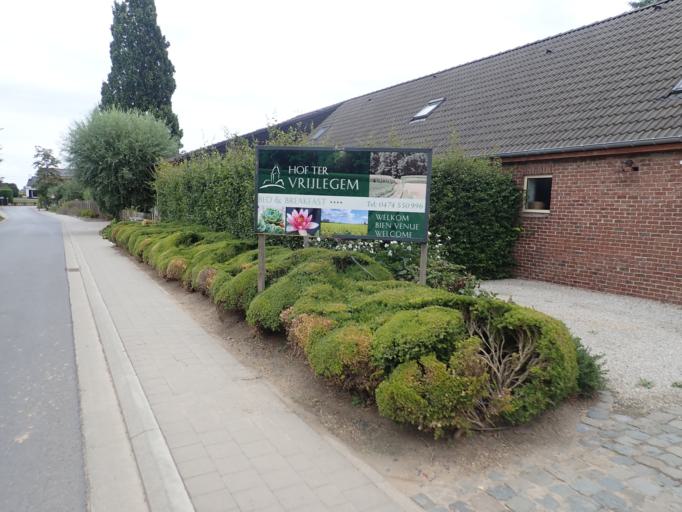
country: BE
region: Flanders
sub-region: Provincie Vlaams-Brabant
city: Asse
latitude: 50.9331
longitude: 4.2094
